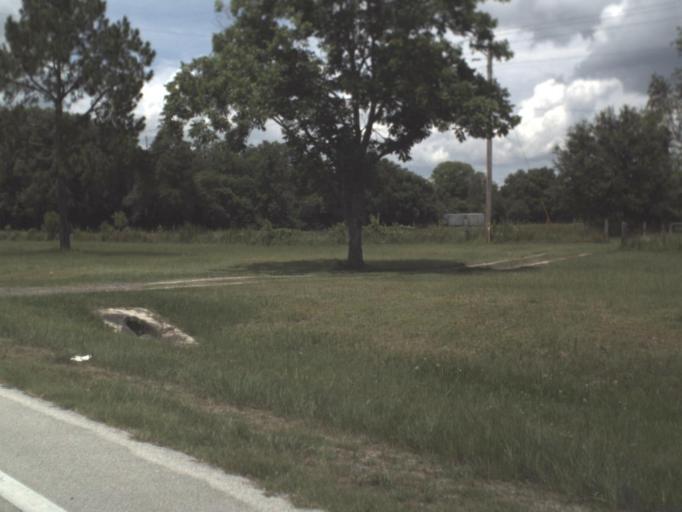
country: US
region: Florida
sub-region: Alachua County
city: Newberry
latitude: 29.7162
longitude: -82.6071
